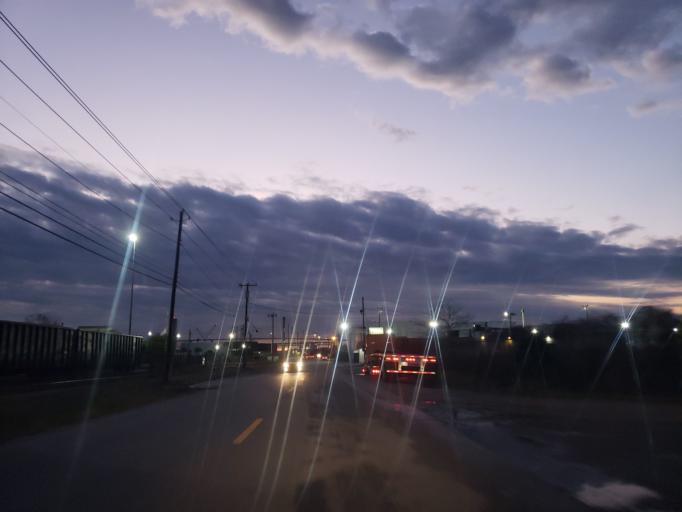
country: US
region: Georgia
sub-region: Chatham County
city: Savannah
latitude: 32.0959
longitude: -81.1151
